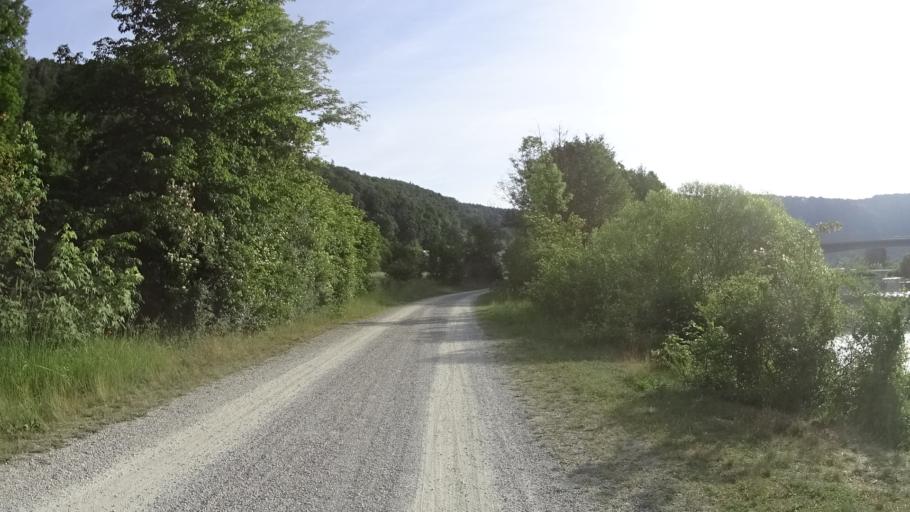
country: DE
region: Bavaria
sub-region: Lower Bavaria
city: Riedenburg
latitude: 48.9898
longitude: 11.6723
